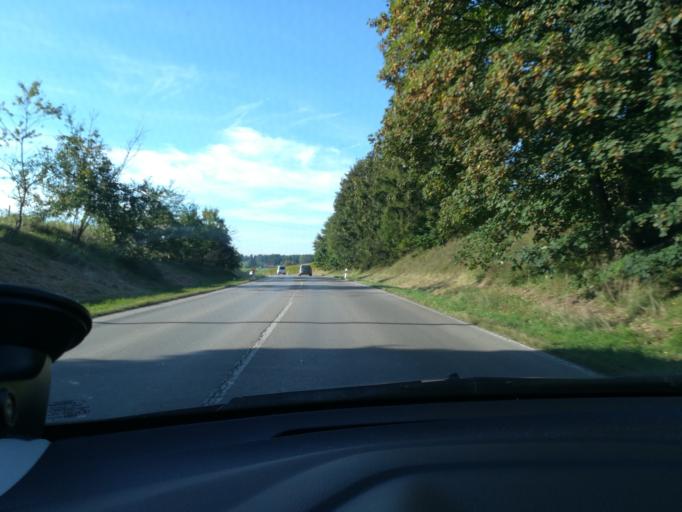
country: DE
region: Bavaria
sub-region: Upper Bavaria
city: Miesbach
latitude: 47.8176
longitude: 11.8377
